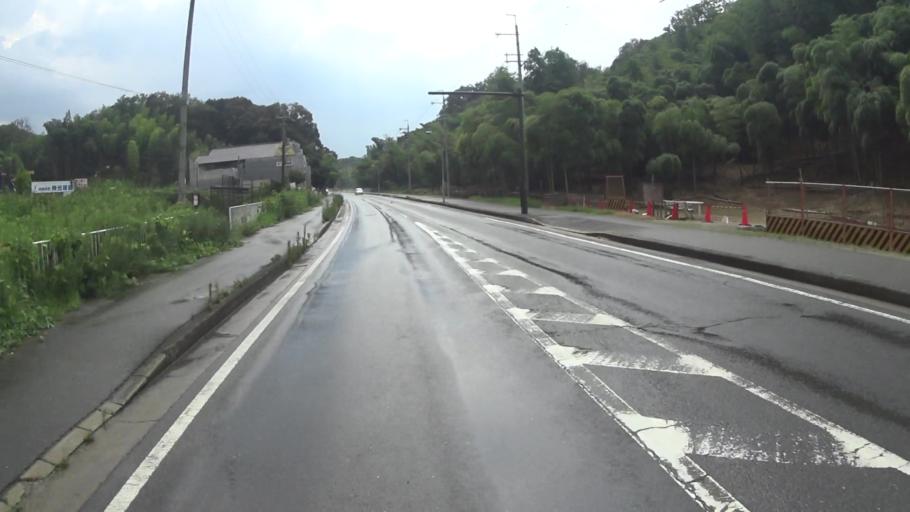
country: JP
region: Kyoto
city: Tanabe
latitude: 34.8136
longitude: 135.7645
